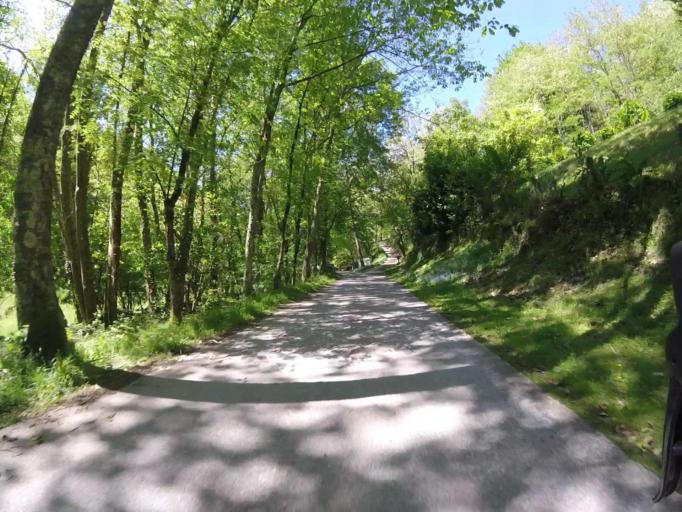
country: ES
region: Navarre
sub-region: Provincia de Navarra
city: Lesaka
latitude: 43.2451
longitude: -1.7264
